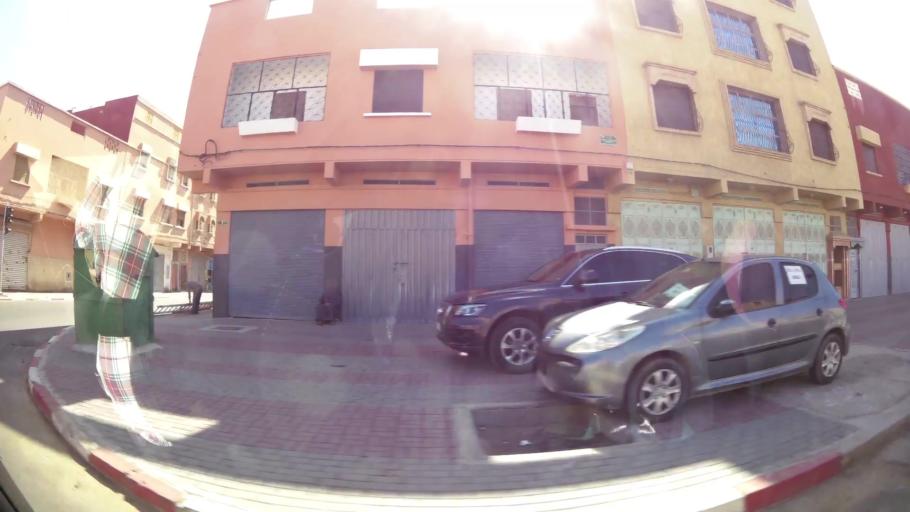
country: MA
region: Souss-Massa-Draa
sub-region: Inezgane-Ait Mellou
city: Inezgane
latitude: 30.3459
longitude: -9.5074
